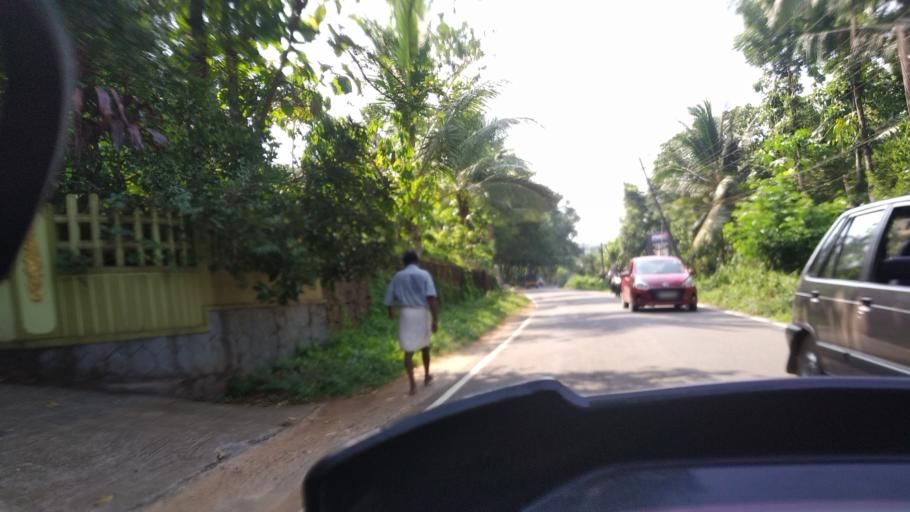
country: IN
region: Kerala
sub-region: Ernakulam
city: Piravam
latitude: 9.8117
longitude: 76.5688
